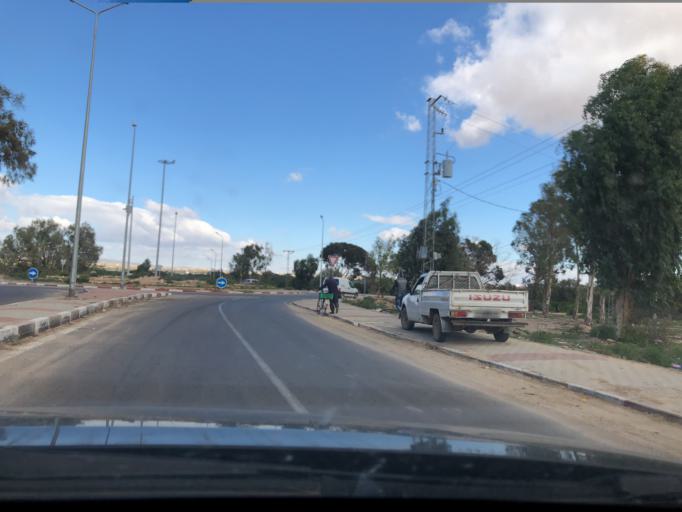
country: TN
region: Al Qasrayn
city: Kasserine
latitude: 35.1966
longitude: 8.8756
